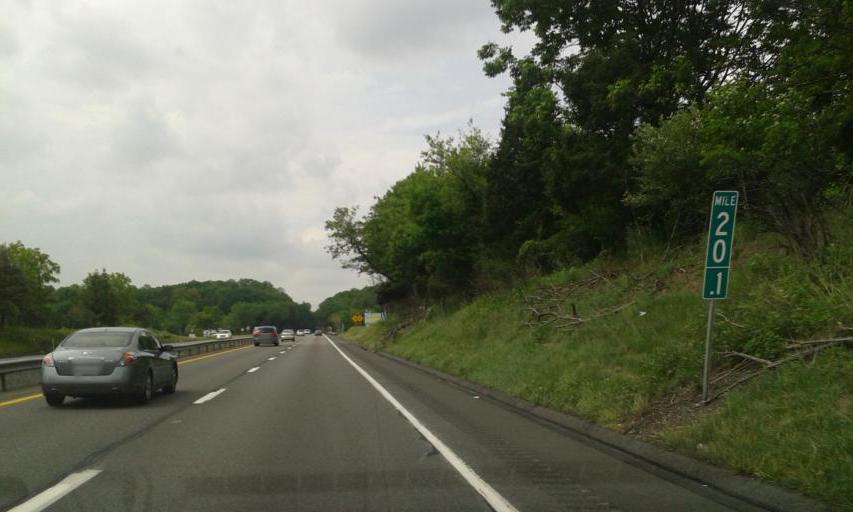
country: US
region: Pennsylvania
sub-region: Monroe County
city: Saylorsburg
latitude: 40.8876
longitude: -75.3102
